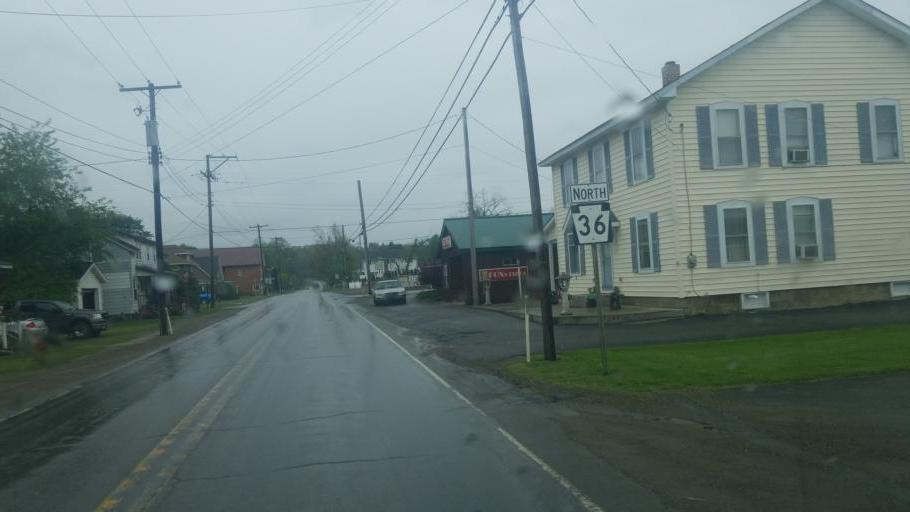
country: US
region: Pennsylvania
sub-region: Forest County
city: Tionesta
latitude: 41.3840
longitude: -79.3219
